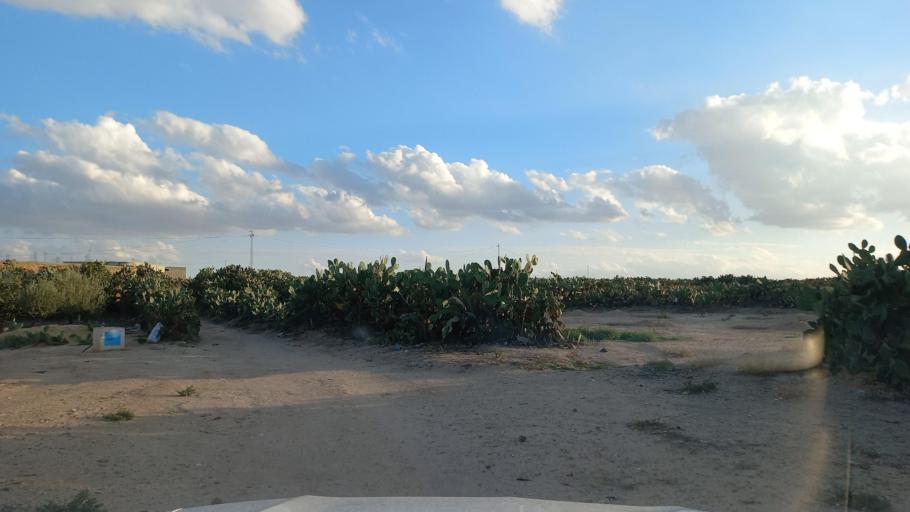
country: TN
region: Al Qasrayn
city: Sbiba
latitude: 35.3795
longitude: 9.0508
